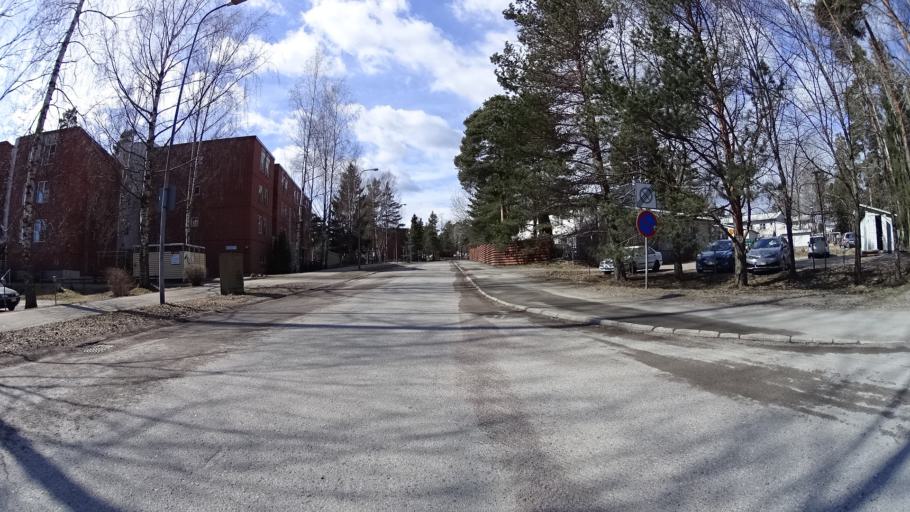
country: FI
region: Uusimaa
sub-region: Helsinki
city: Kilo
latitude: 60.2120
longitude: 24.7727
